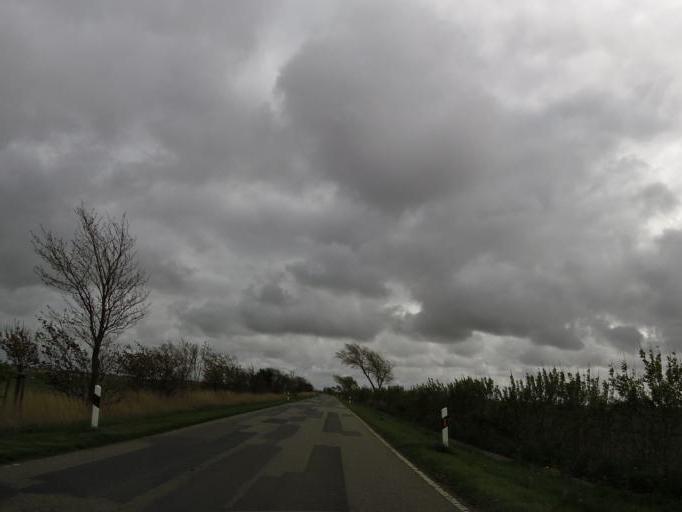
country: DE
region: Schleswig-Holstein
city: Galmsbull
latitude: 54.7628
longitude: 8.7520
